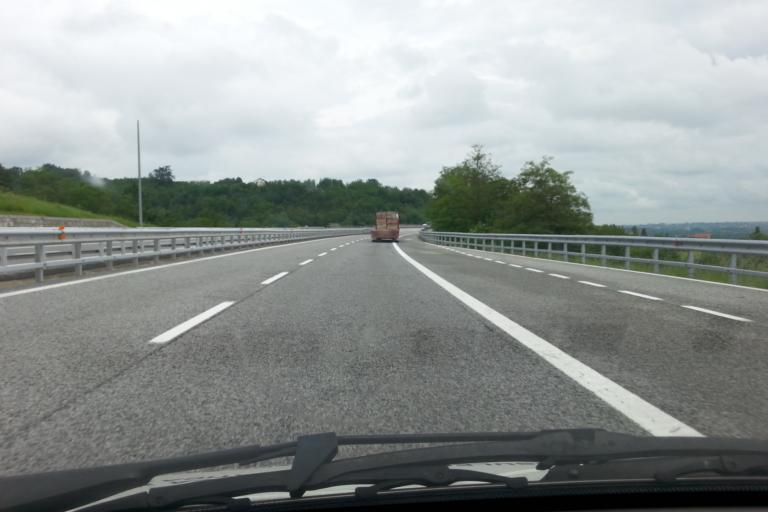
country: IT
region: Piedmont
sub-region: Provincia di Cuneo
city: Bastia Mondovi
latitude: 44.4174
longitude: 7.8940
